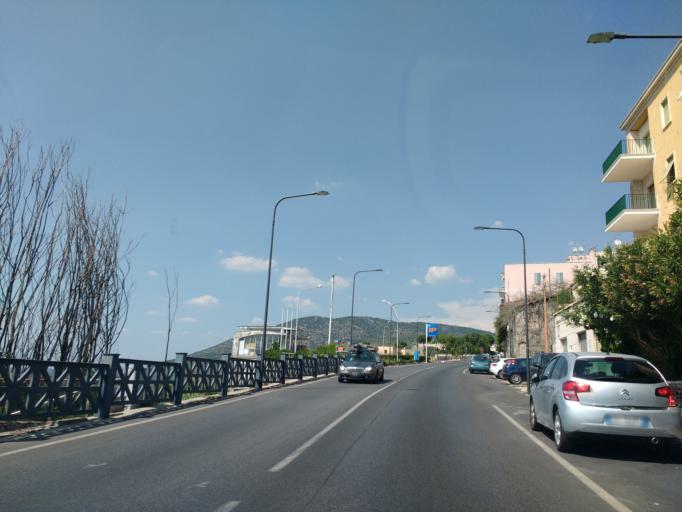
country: IT
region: Latium
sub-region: Citta metropolitana di Roma Capitale
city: Tivoli
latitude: 41.9558
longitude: 12.7922
